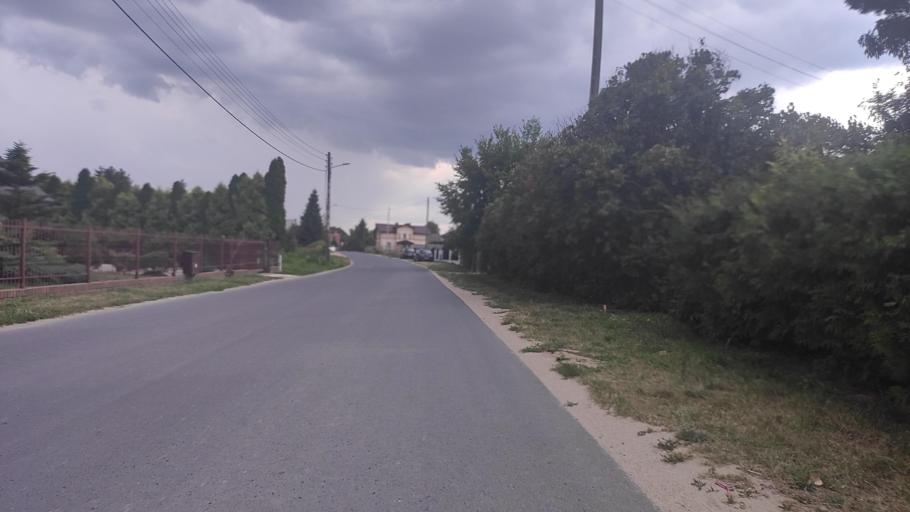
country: PL
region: Greater Poland Voivodeship
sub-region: Powiat poznanski
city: Swarzedz
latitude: 52.3891
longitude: 17.1175
